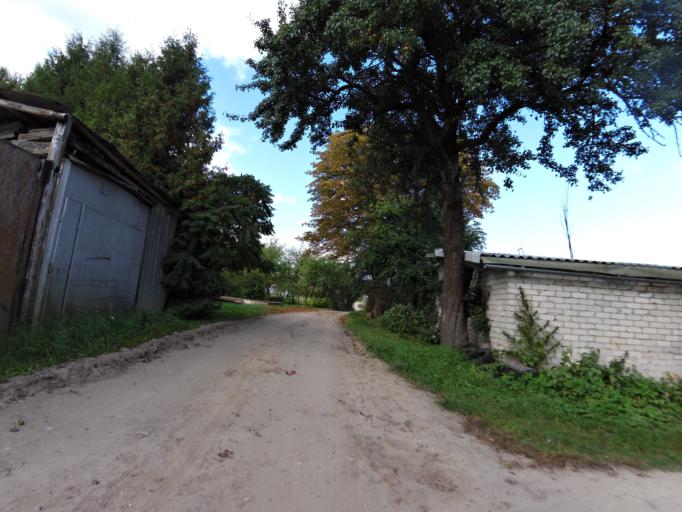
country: LT
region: Vilnius County
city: Pilaite
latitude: 54.7016
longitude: 25.1563
